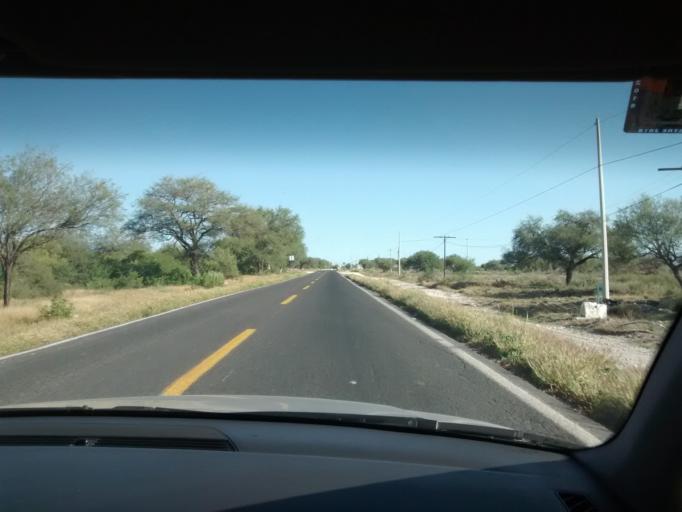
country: MX
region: Puebla
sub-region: Tepanco de Lopez
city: San Andres Cacaloapan
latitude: 18.5706
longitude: -97.5744
